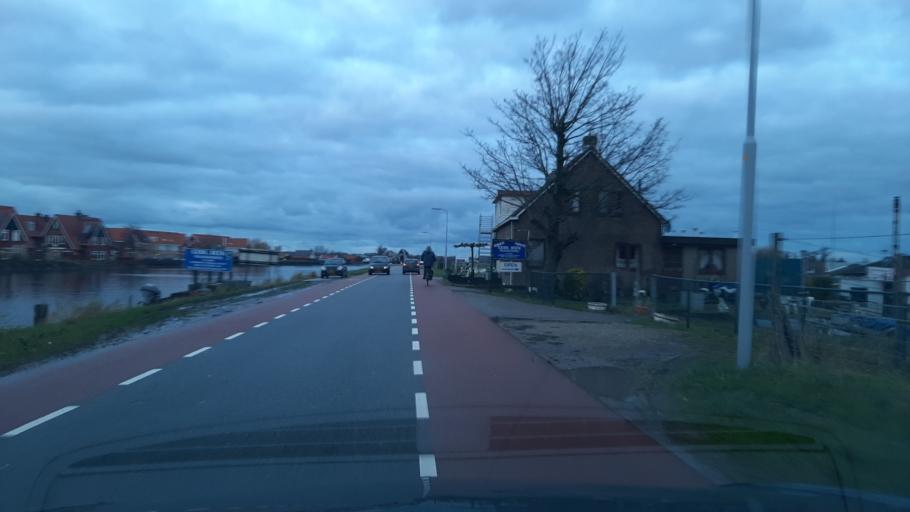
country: NL
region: South Holland
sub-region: Gemeente Hillegom
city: Hillegom
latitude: 52.2944
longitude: 4.5972
